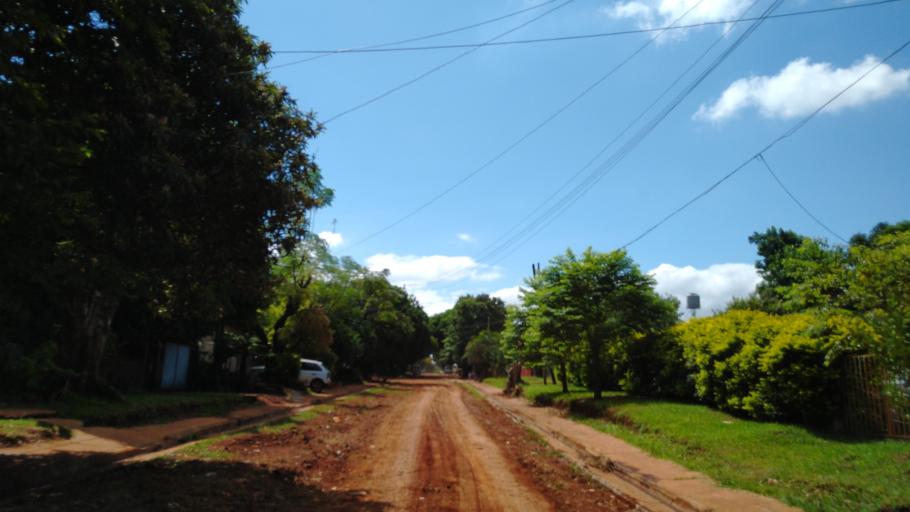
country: AR
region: Misiones
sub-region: Departamento de Capital
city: Posadas
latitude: -27.3904
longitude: -55.9208
